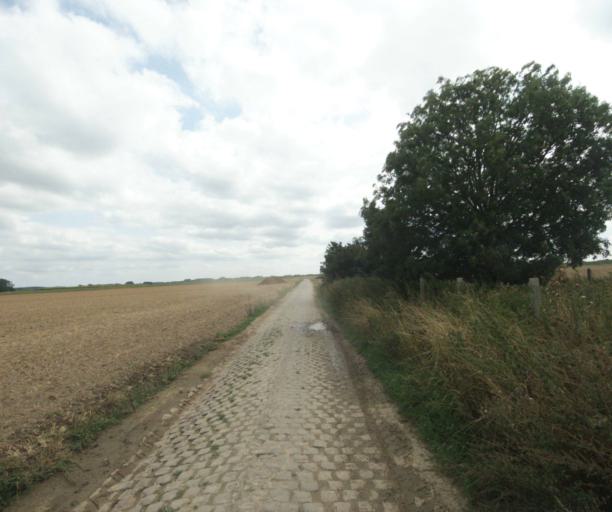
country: FR
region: Nord-Pas-de-Calais
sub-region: Departement du Nord
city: Gruson
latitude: 50.5891
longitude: 3.2302
